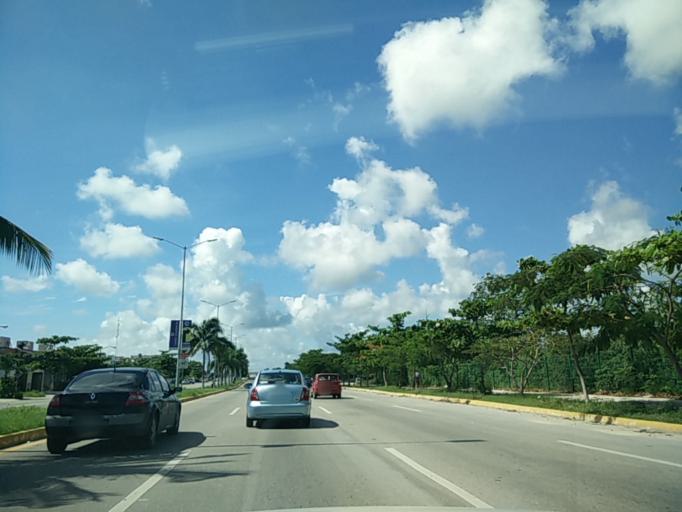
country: MX
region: Quintana Roo
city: Playa del Carmen
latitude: 20.6675
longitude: -87.0674
